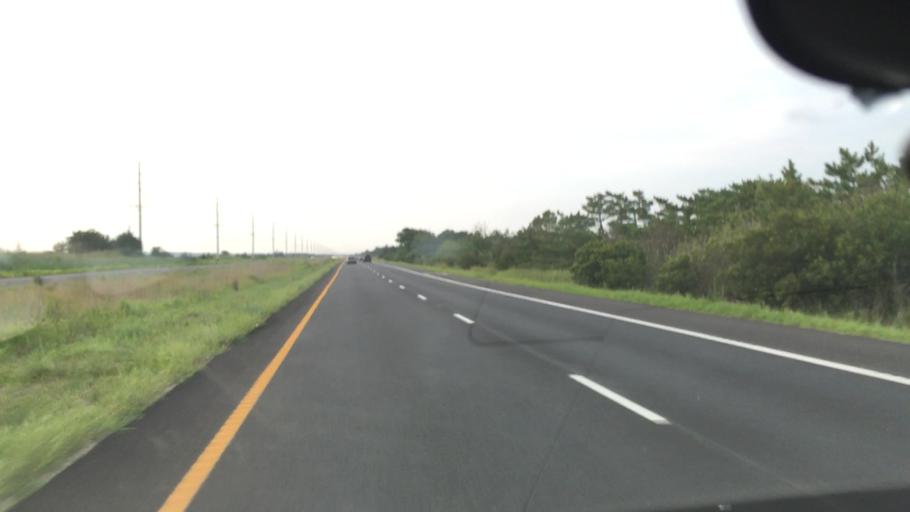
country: US
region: Delaware
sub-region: Sussex County
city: Rehoboth Beach
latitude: 38.6516
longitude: -75.0688
